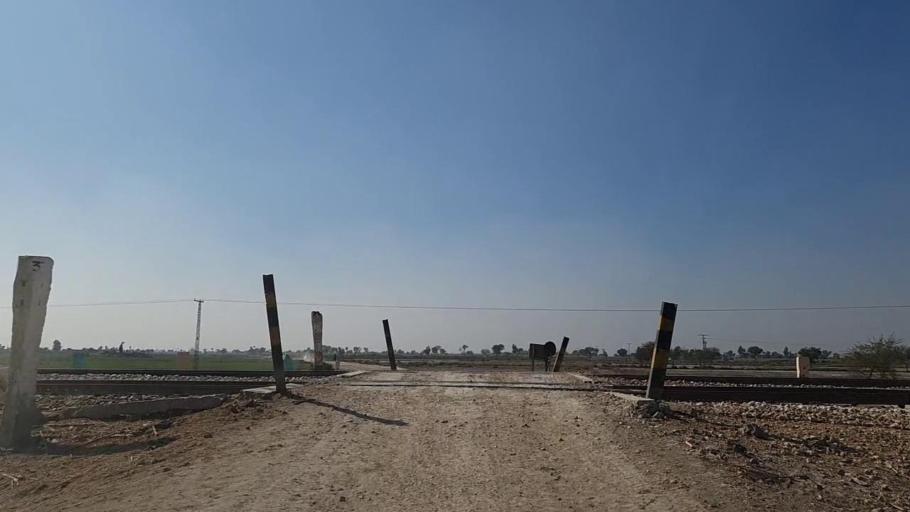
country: PK
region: Sindh
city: Bandhi
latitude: 26.5322
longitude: 68.3066
